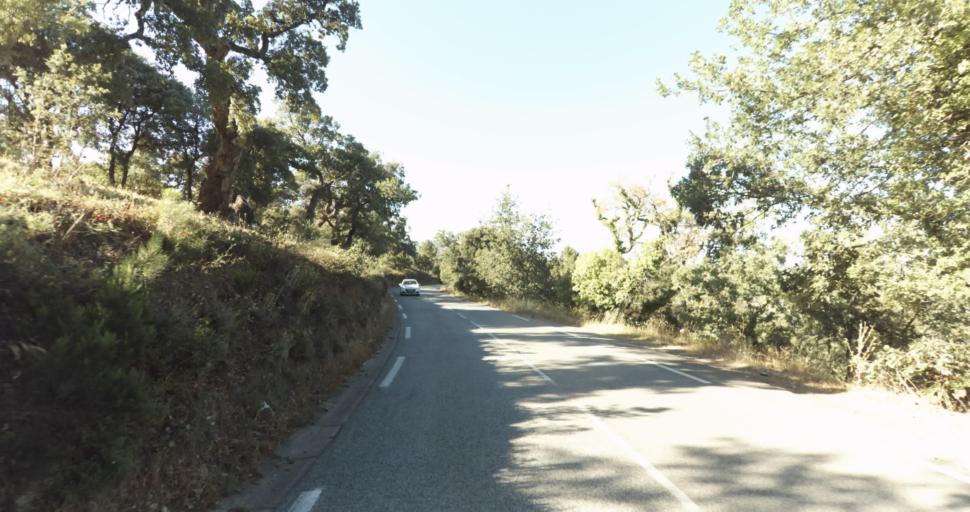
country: FR
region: Provence-Alpes-Cote d'Azur
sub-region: Departement du Var
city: Gassin
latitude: 43.2334
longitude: 6.5857
